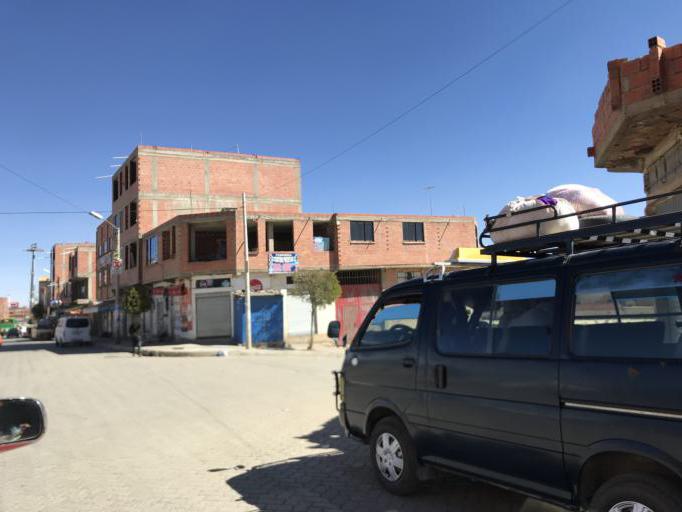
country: BO
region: La Paz
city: La Paz
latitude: -16.4872
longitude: -68.2008
